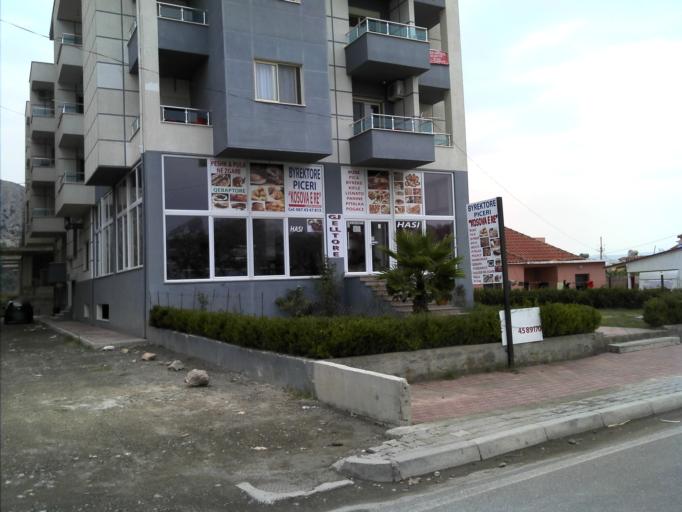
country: AL
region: Lezhe
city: Shengjin
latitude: 41.8037
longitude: 19.6004
